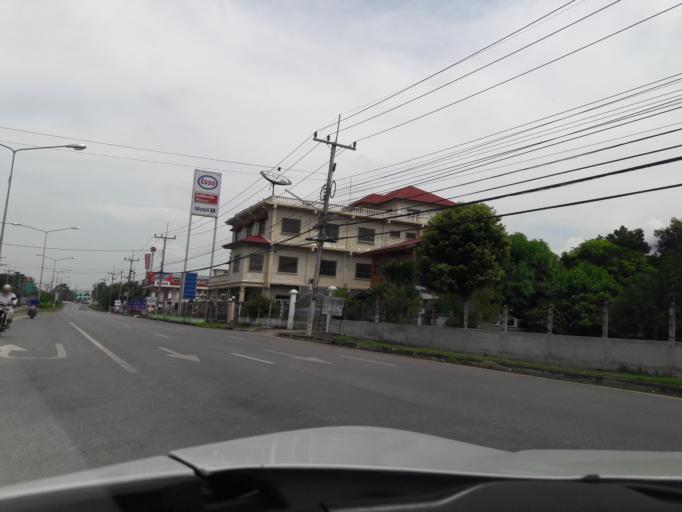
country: TH
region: Lop Buri
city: Ban Mi
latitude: 15.0463
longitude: 100.5599
